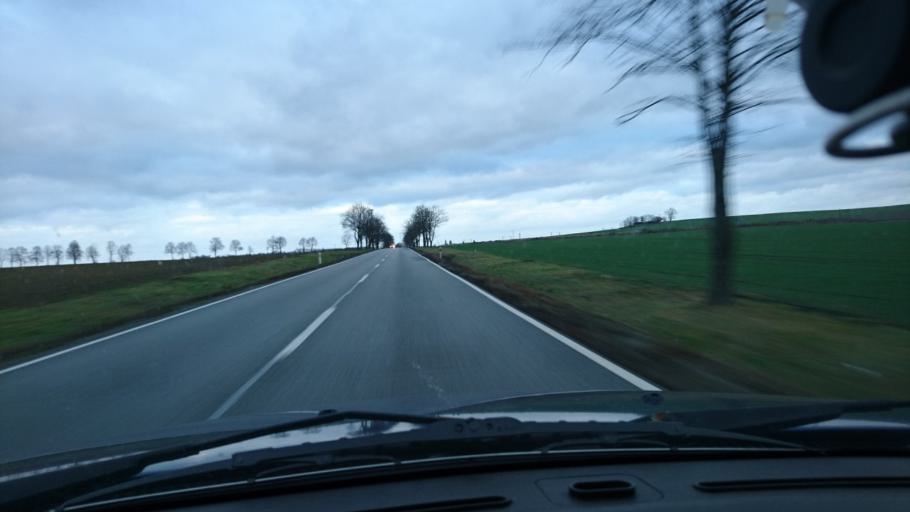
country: PL
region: Opole Voivodeship
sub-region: Powiat kluczborski
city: Byczyna
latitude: 51.0919
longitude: 18.2014
